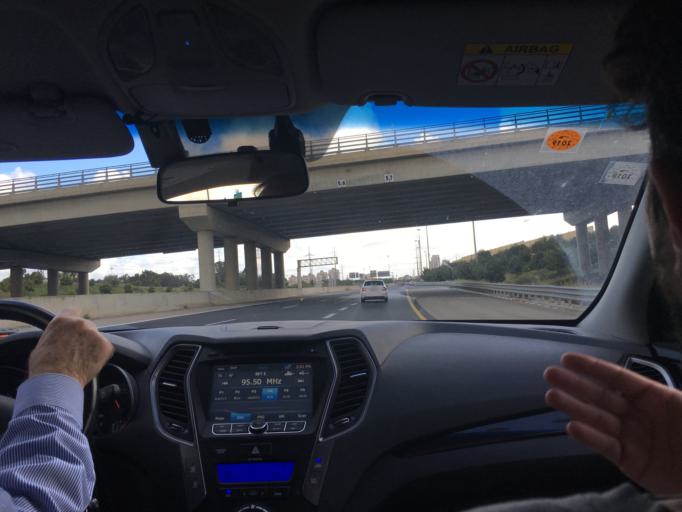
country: IL
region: Central District
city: Rishon LeZiyyon
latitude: 31.9554
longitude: 34.7854
